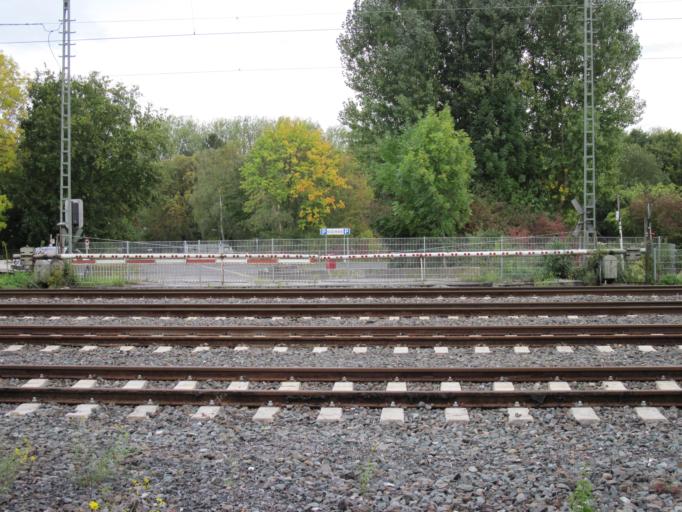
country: DE
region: North Rhine-Westphalia
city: Lanstrop
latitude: 51.5600
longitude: 7.5239
